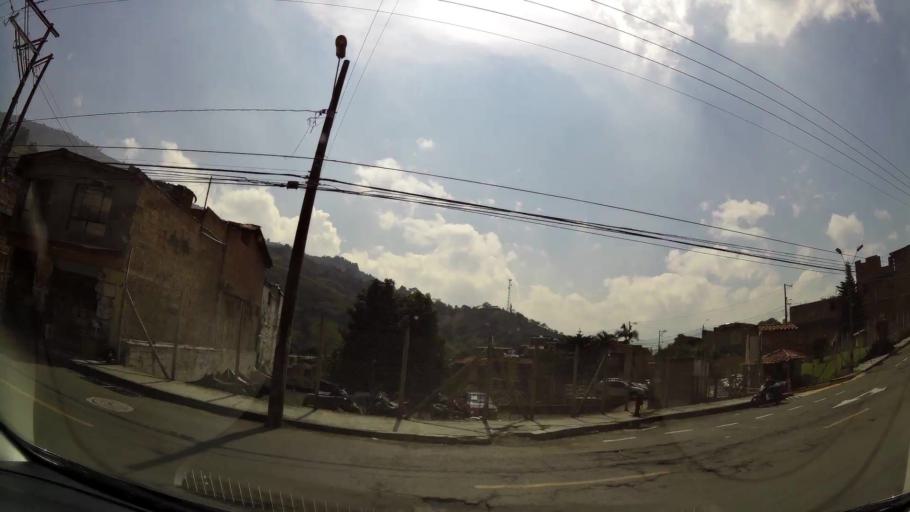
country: CO
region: Antioquia
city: La Estrella
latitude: 6.1854
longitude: -75.6410
